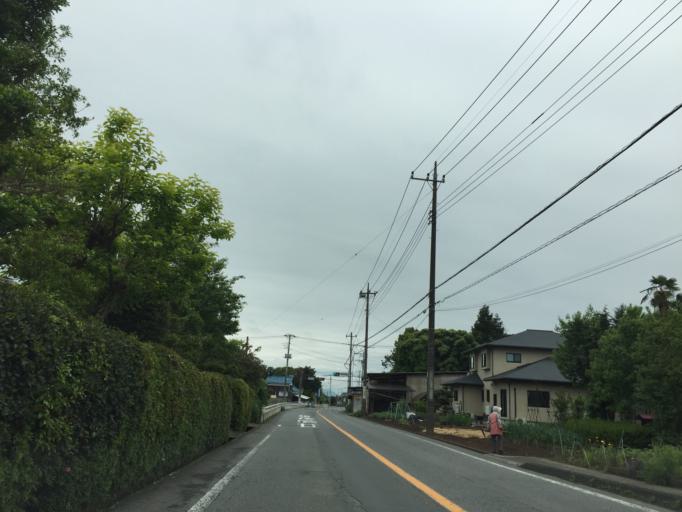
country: JP
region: Shizuoka
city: Mishima
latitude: 35.1840
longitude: 138.9203
